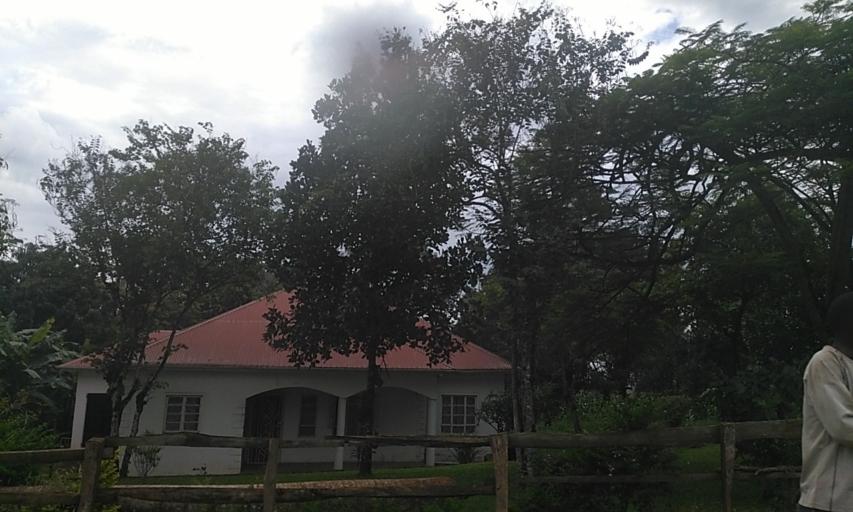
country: UG
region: Central Region
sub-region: Wakiso District
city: Bweyogerere
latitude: 0.3960
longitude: 32.6971
